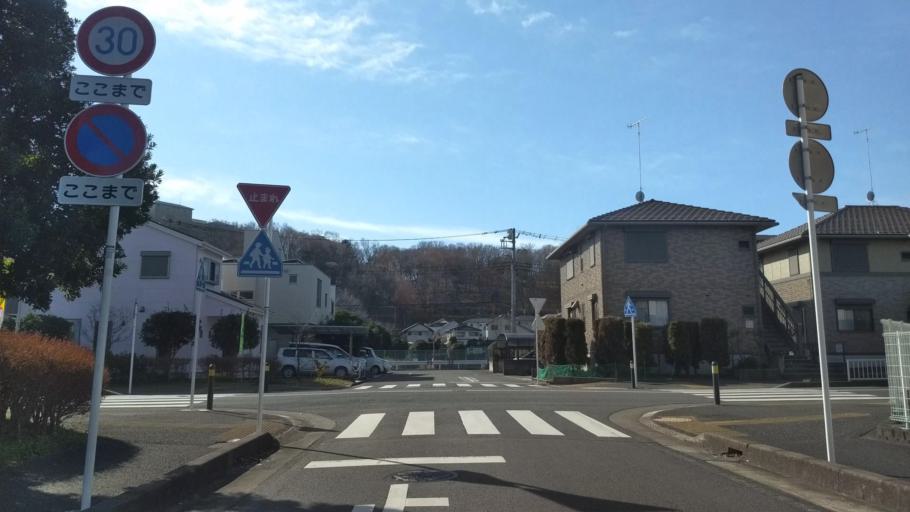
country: JP
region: Kanagawa
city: Hadano
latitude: 35.3582
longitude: 139.2321
